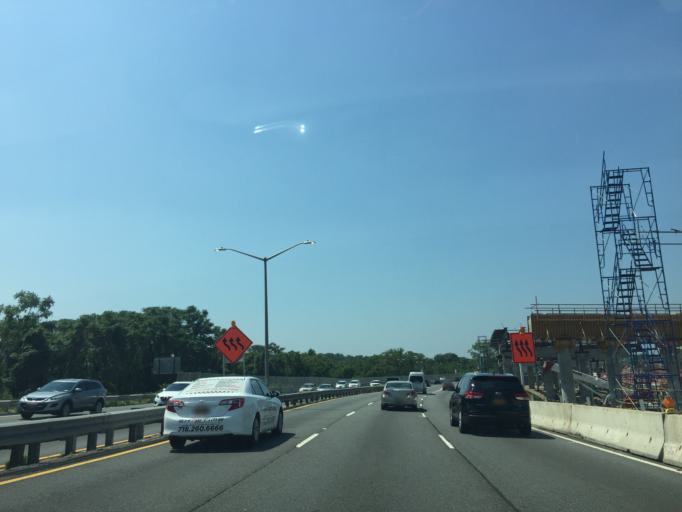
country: US
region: New York
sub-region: Kings County
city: East New York
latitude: 40.6032
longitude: -73.8992
